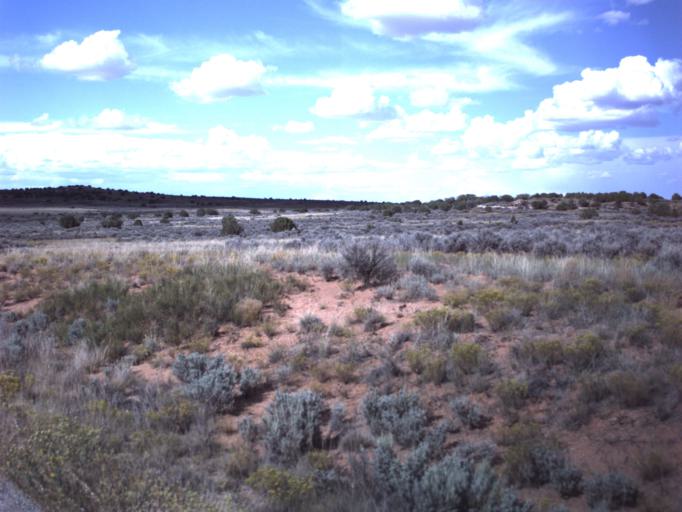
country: US
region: Utah
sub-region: Grand County
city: Moab
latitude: 38.5181
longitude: -109.7307
